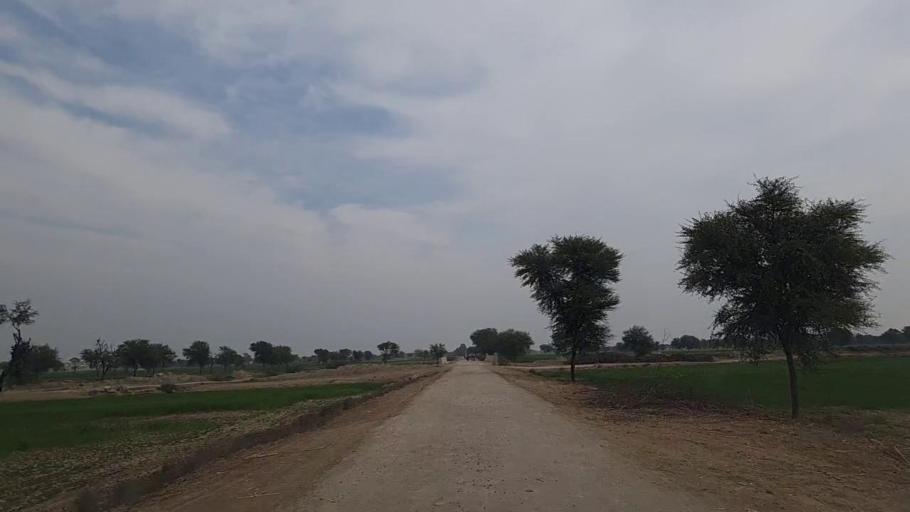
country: PK
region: Sindh
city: Daur
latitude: 26.4449
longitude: 68.4710
